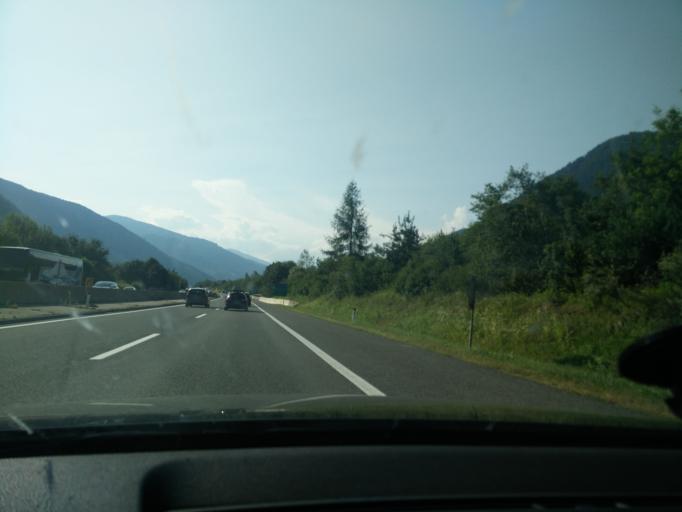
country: AT
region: Carinthia
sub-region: Villach Stadt
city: Villach
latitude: 46.6450
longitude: 13.8829
